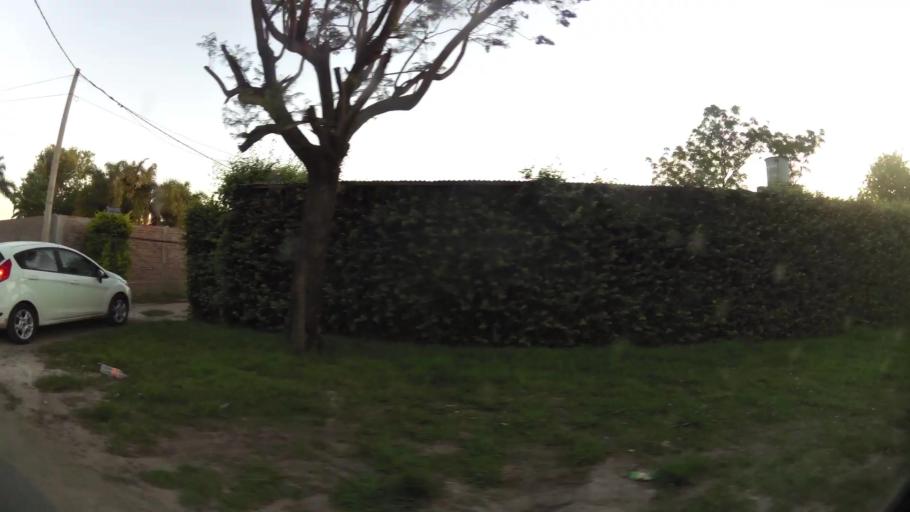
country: AR
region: Santa Fe
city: Santa Fe de la Vera Cruz
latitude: -31.5923
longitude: -60.6942
